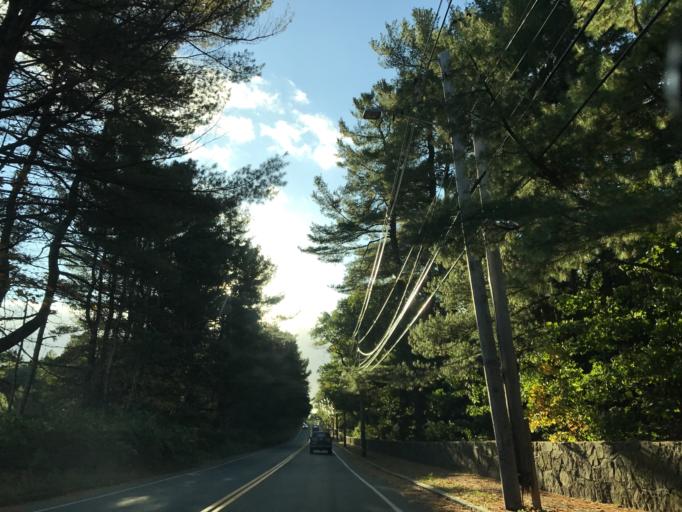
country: US
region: Massachusetts
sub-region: Suffolk County
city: Jamaica Plain
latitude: 42.3051
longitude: -71.1463
